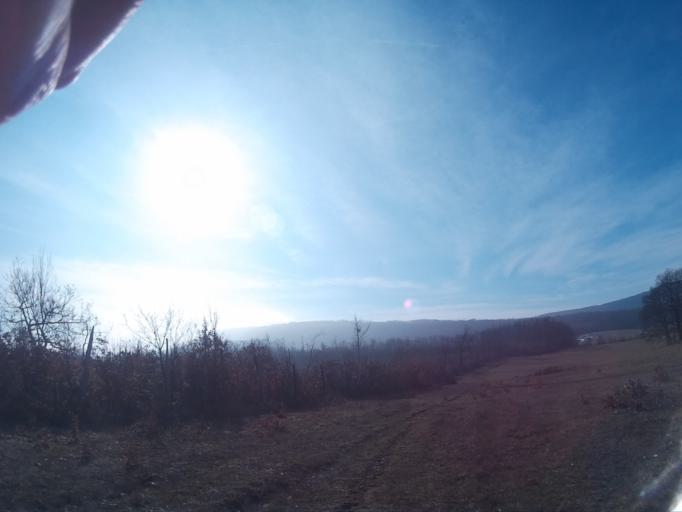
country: HU
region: Komarom-Esztergom
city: Tarjan
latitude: 47.6252
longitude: 18.4788
